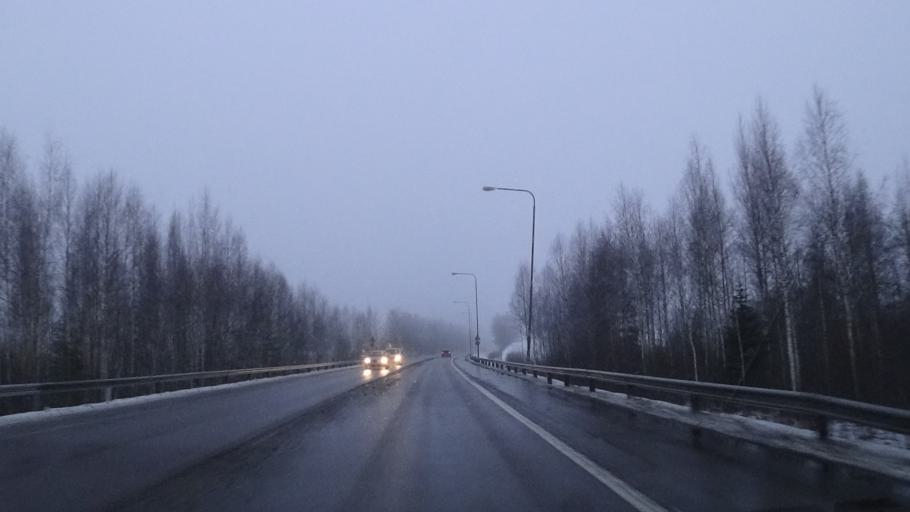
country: FI
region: Paijanne Tavastia
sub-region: Lahti
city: Hollola
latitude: 60.9817
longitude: 25.4671
